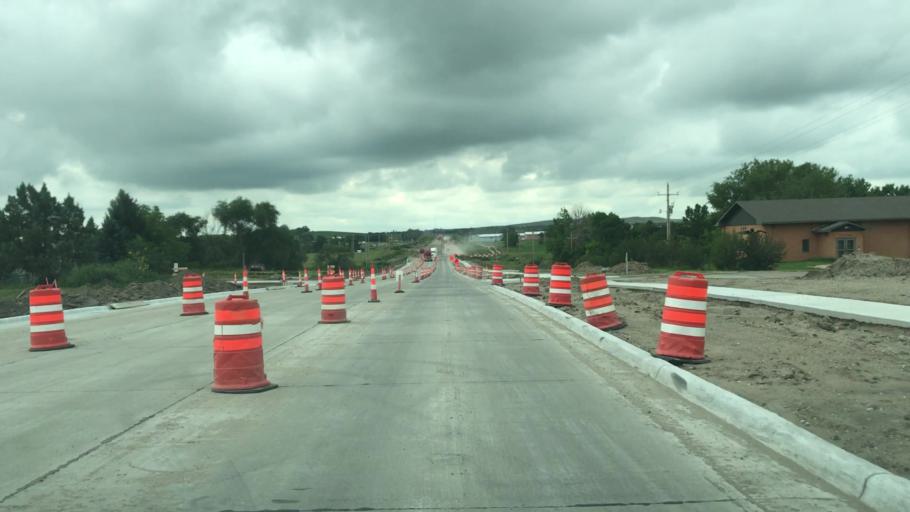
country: US
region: South Dakota
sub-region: Todd County
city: Mission
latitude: 43.3052
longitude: -100.6527
